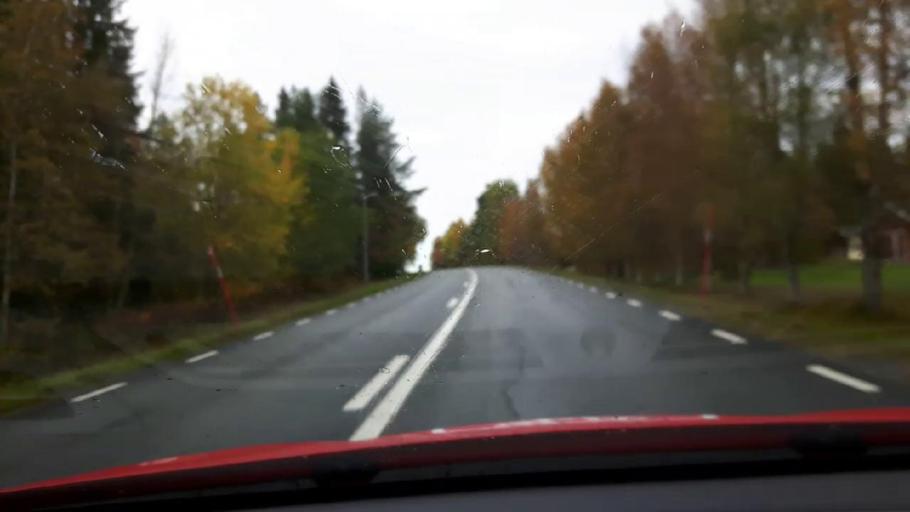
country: SE
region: Jaemtland
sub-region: Krokoms Kommun
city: Krokom
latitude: 63.0980
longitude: 14.3024
